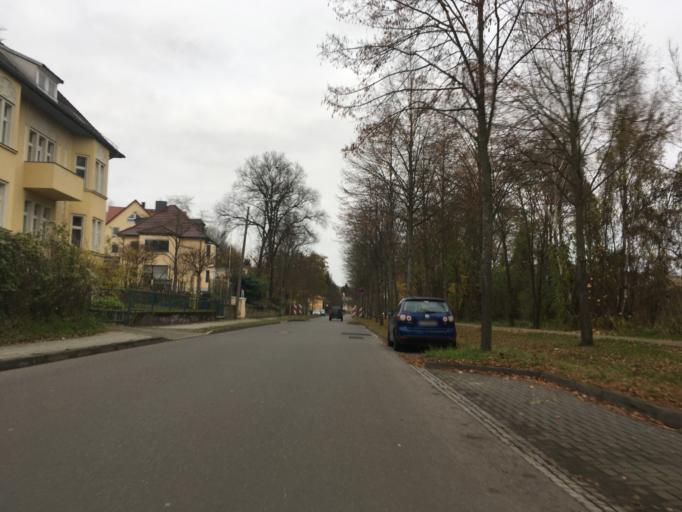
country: DE
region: Brandenburg
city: Frankfurt (Oder)
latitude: 52.3210
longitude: 14.5538
